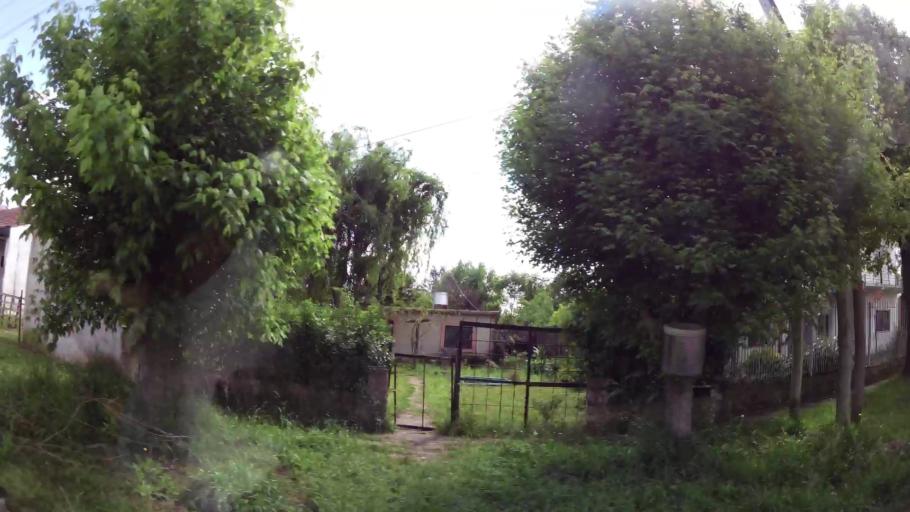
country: AR
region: Buenos Aires
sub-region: Partido de Quilmes
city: Quilmes
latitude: -34.8362
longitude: -58.1721
